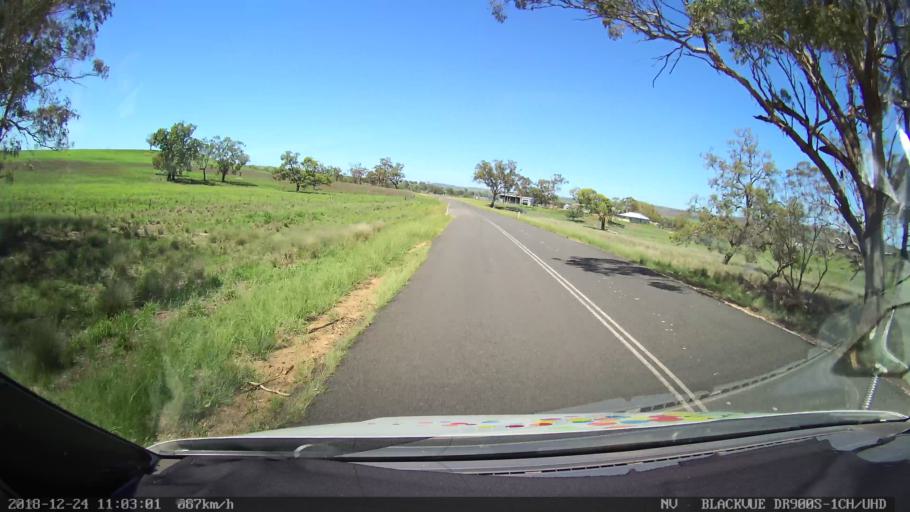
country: AU
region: New South Wales
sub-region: Upper Hunter Shire
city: Merriwa
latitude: -32.0915
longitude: 150.3703
